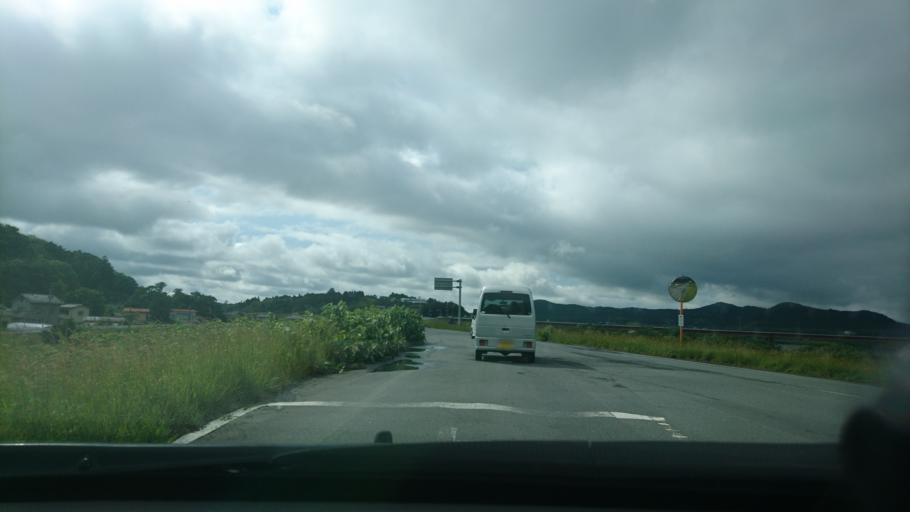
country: JP
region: Miyagi
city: Ishinomaki
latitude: 38.5101
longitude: 141.3095
